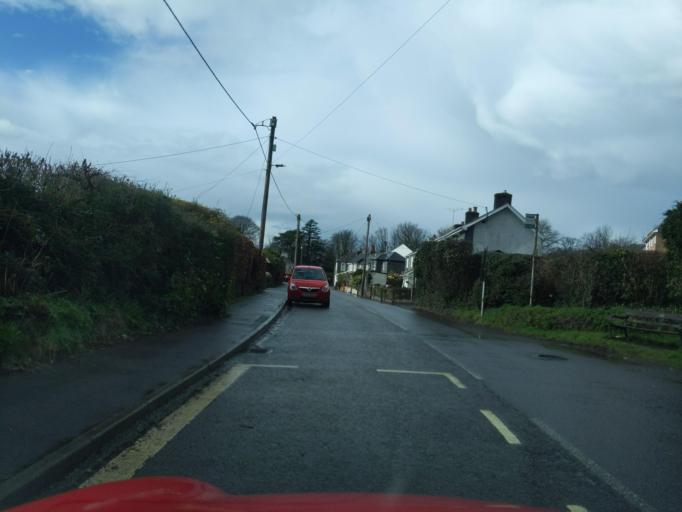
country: GB
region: England
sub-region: Devon
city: Tavistock
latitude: 50.5342
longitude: -4.1308
